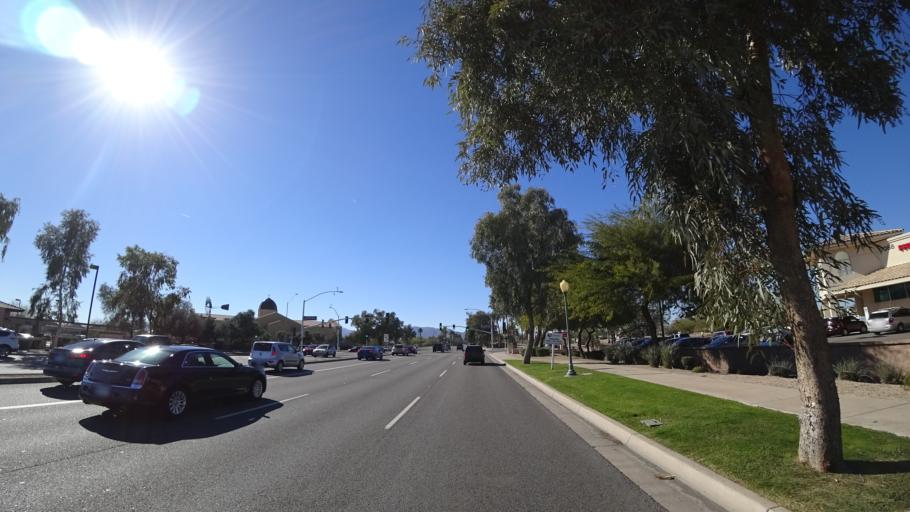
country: US
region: Arizona
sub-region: Maricopa County
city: Sun City West
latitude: 33.6390
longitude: -112.4258
